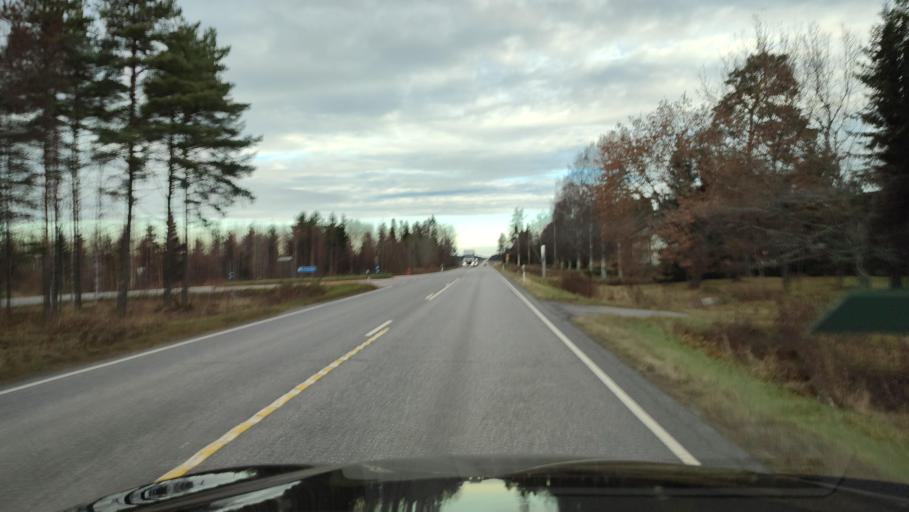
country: FI
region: Ostrobothnia
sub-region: Sydosterbotten
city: Naerpes
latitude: 62.4346
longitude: 21.4243
